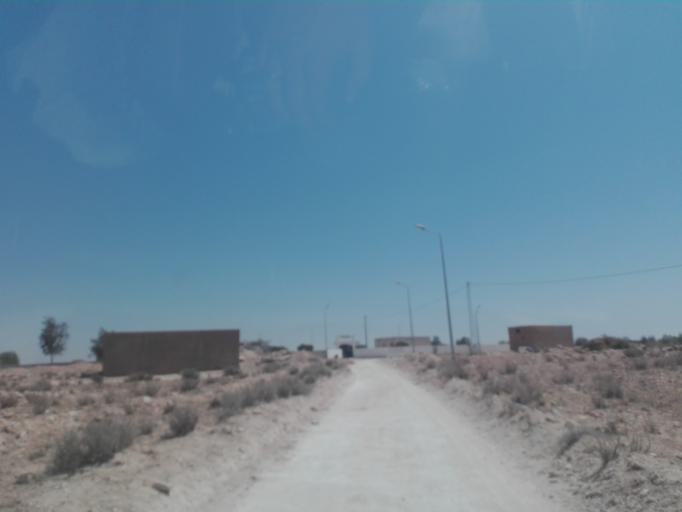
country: TN
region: Safaqis
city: Skhira
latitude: 34.4144
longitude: 9.9501
